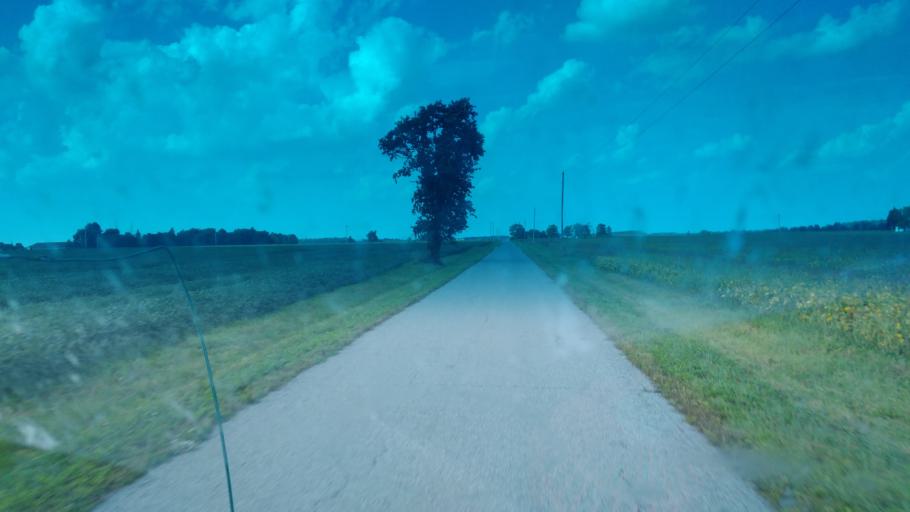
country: US
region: Ohio
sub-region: Hancock County
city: Arlington
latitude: 40.8592
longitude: -83.5855
